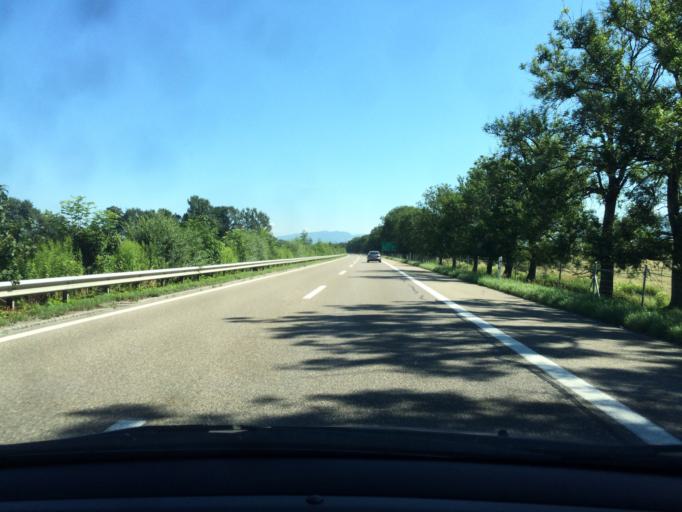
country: AT
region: Vorarlberg
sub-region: Politischer Bezirk Feldkirch
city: Mader
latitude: 47.3695
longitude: 9.6250
